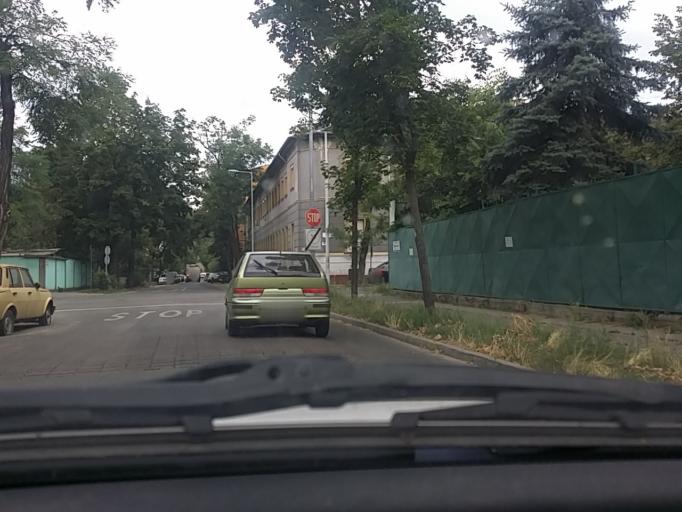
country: HU
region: Budapest
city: Budapest X. keruelet
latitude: 47.4878
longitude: 19.1303
